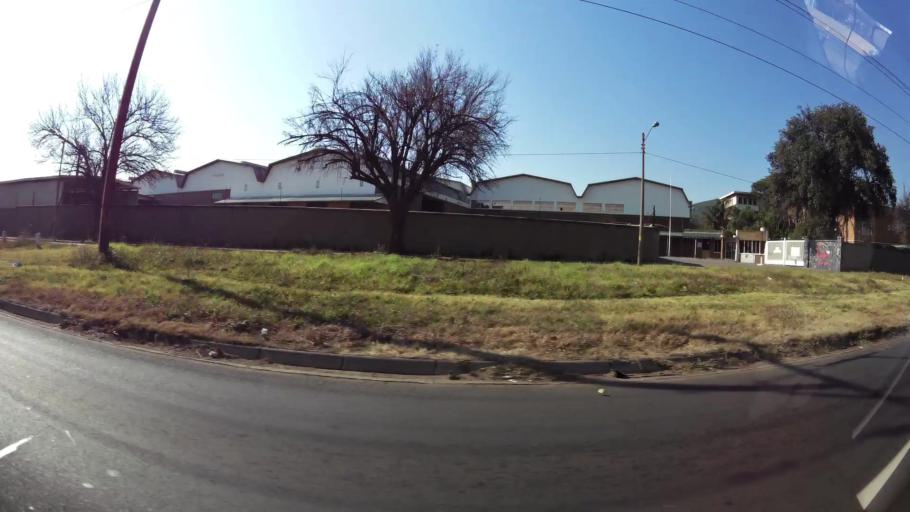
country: ZA
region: Gauteng
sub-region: City of Johannesburg Metropolitan Municipality
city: Modderfontein
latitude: -26.1397
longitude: 28.2020
